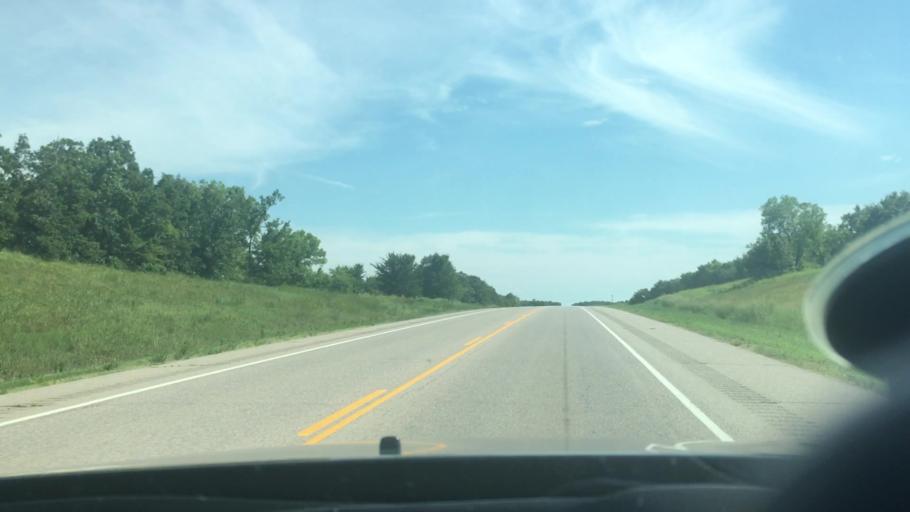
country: US
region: Oklahoma
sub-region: Seminole County
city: Maud
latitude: 35.1178
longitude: -96.6790
